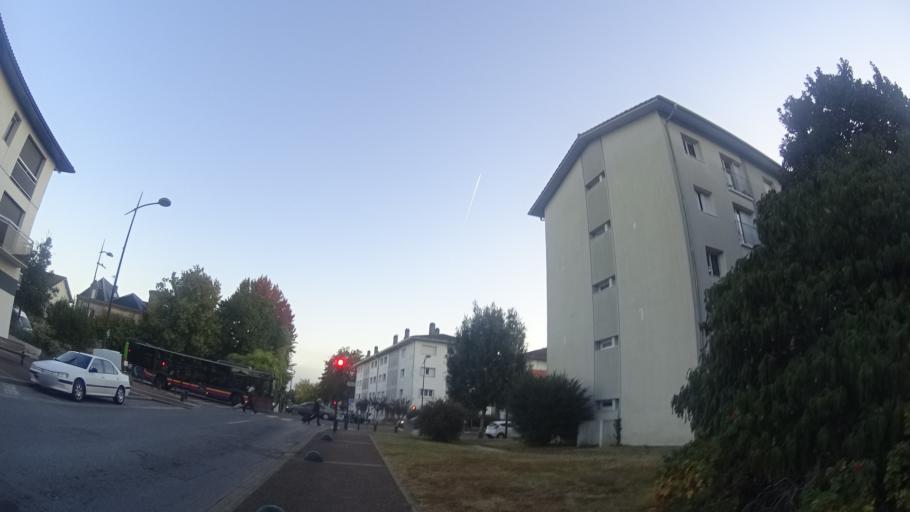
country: FR
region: Aquitaine
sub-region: Departement des Landes
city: Saint-Paul-les-Dax
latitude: 43.7237
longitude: -1.0532
